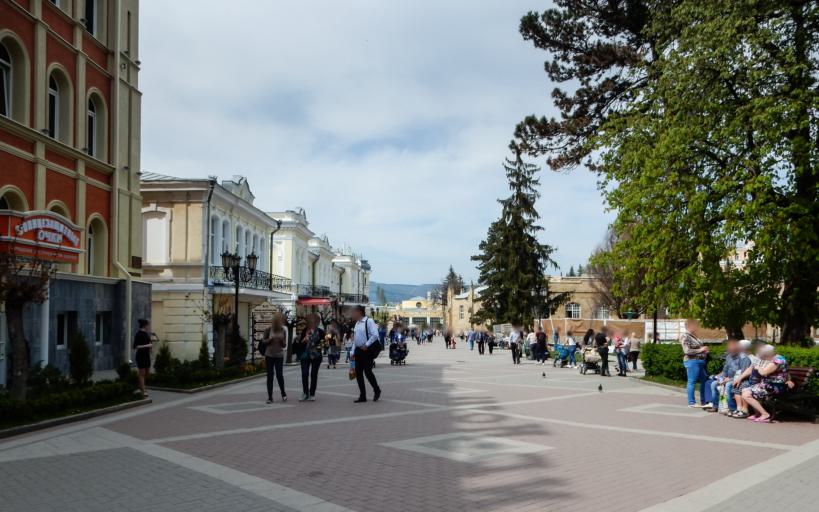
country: RU
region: Stavropol'skiy
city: Kislovodsk
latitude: 43.8995
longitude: 42.7165
